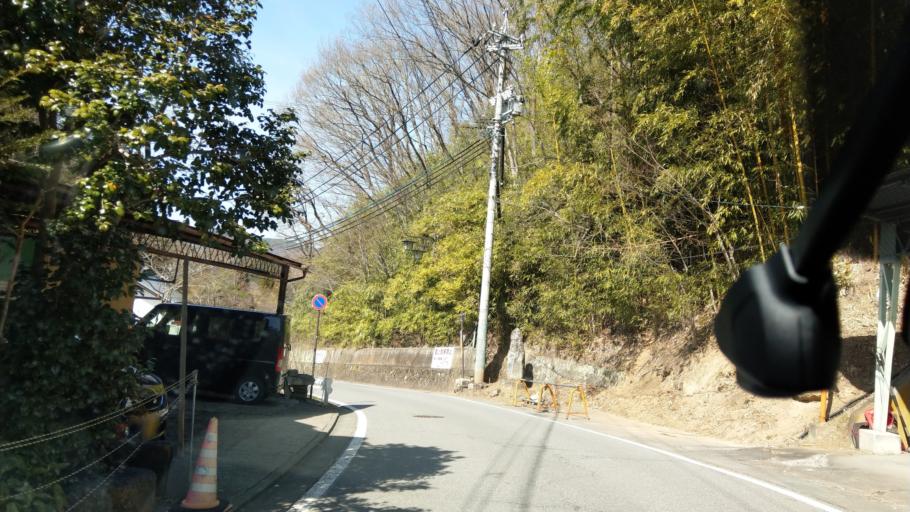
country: JP
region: Nagano
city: Kamimaruko
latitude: 36.3499
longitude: 138.1603
